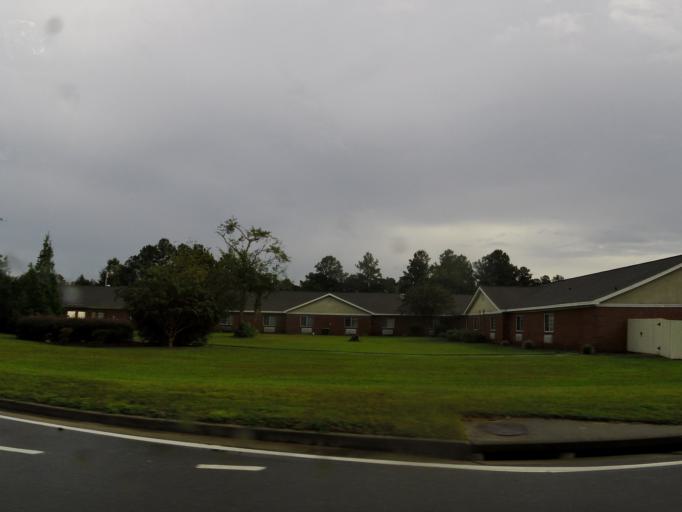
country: US
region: Georgia
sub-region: Long County
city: Ludowici
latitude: 31.7197
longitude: -81.7336
